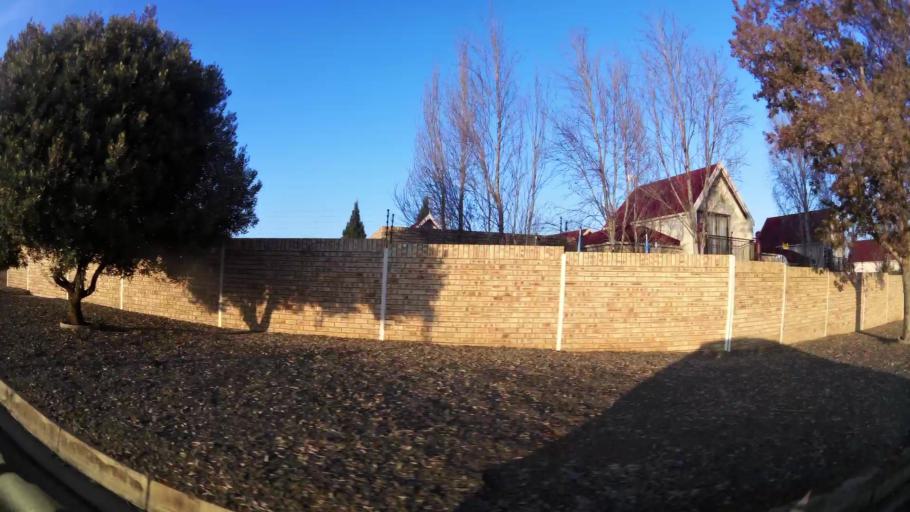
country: ZA
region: Orange Free State
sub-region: Mangaung Metropolitan Municipality
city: Bloemfontein
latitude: -29.1022
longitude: 26.1636
